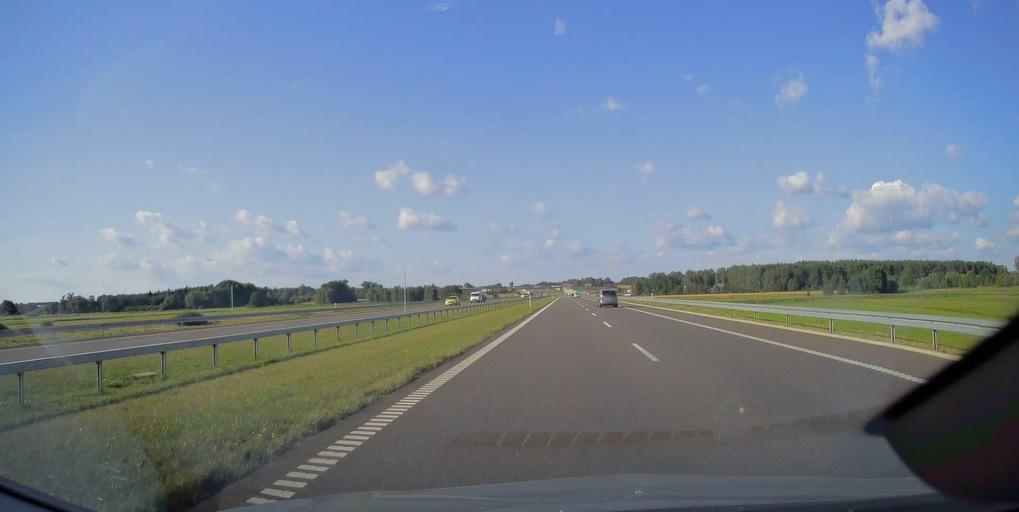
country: PL
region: Masovian Voivodeship
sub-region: Powiat radomski
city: Jedlinsk
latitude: 51.5003
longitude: 21.0786
